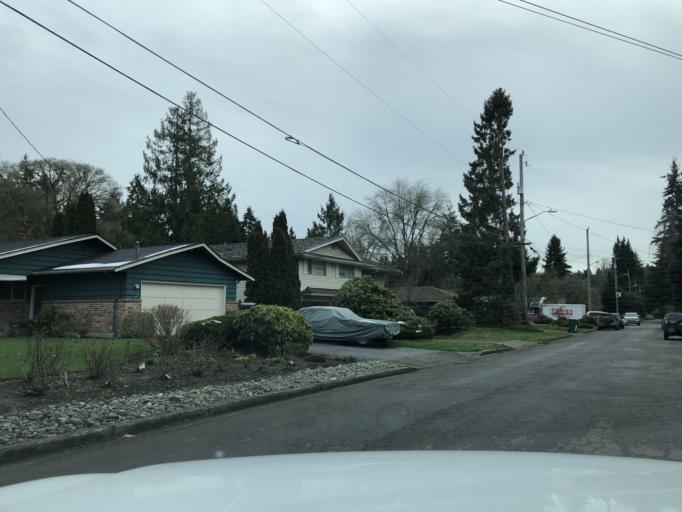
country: US
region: Washington
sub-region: King County
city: Inglewood-Finn Hill
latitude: 47.7038
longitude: -122.2814
